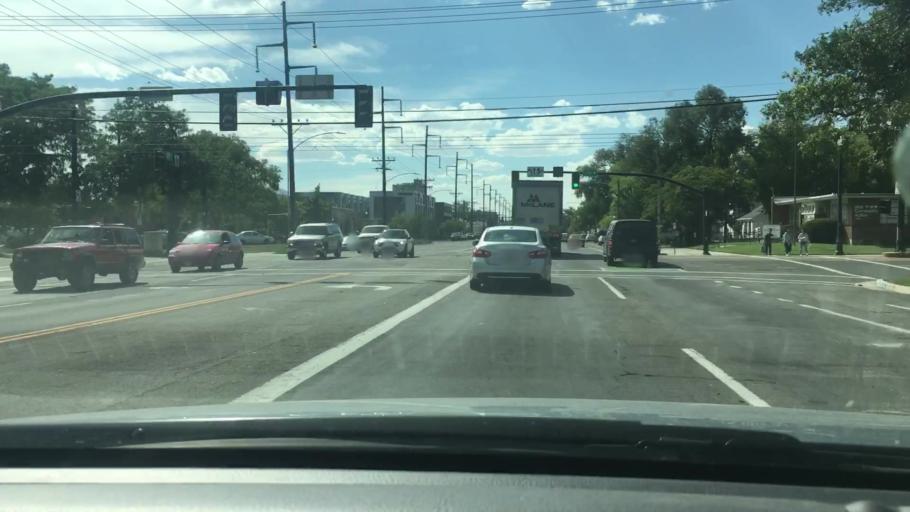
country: US
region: Utah
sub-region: Salt Lake County
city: Salt Lake City
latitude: 40.7520
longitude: -111.8962
